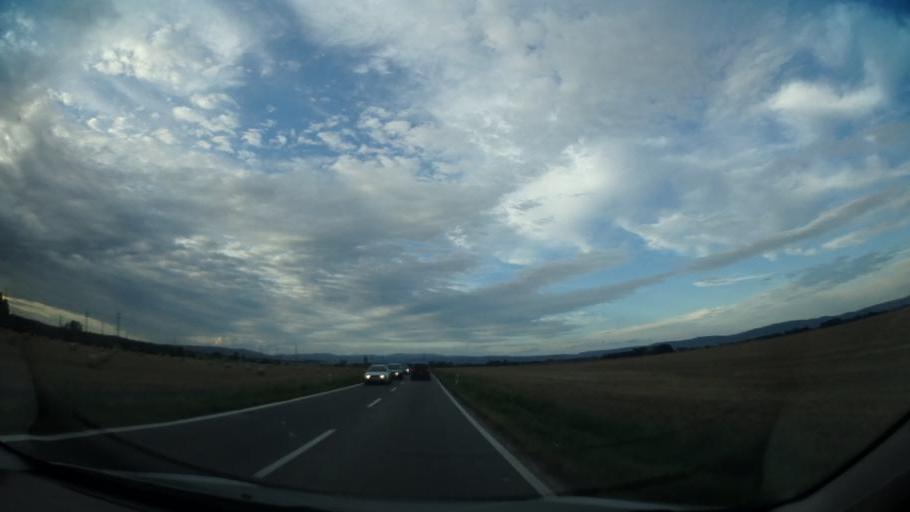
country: CZ
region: Olomoucky
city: Cervenka
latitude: 49.7285
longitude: 17.0823
